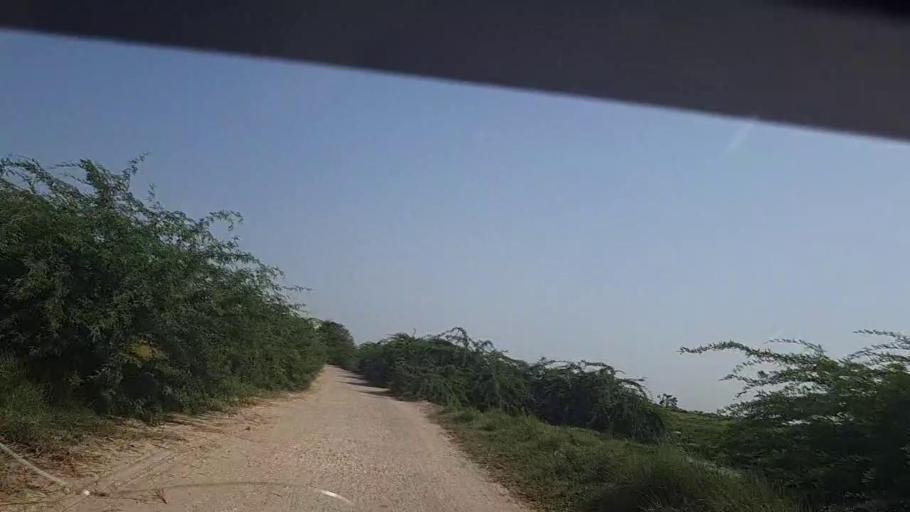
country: PK
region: Sindh
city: Rajo Khanani
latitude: 24.9733
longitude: 68.8695
